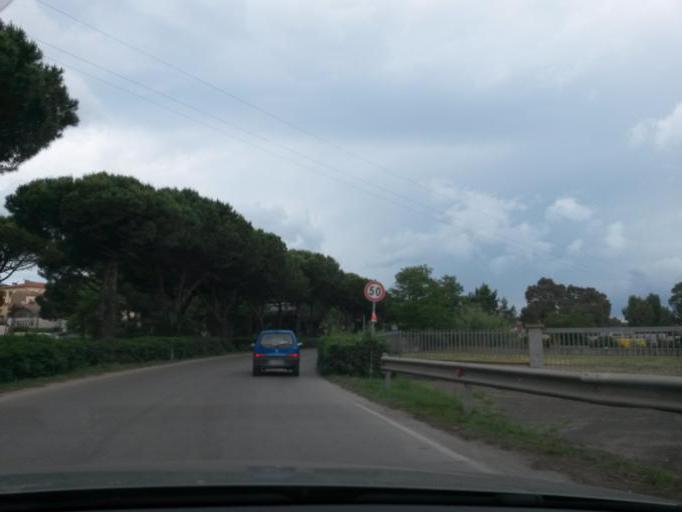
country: IT
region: Tuscany
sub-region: Provincia di Livorno
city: Portoferraio
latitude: 42.8028
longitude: 10.3085
